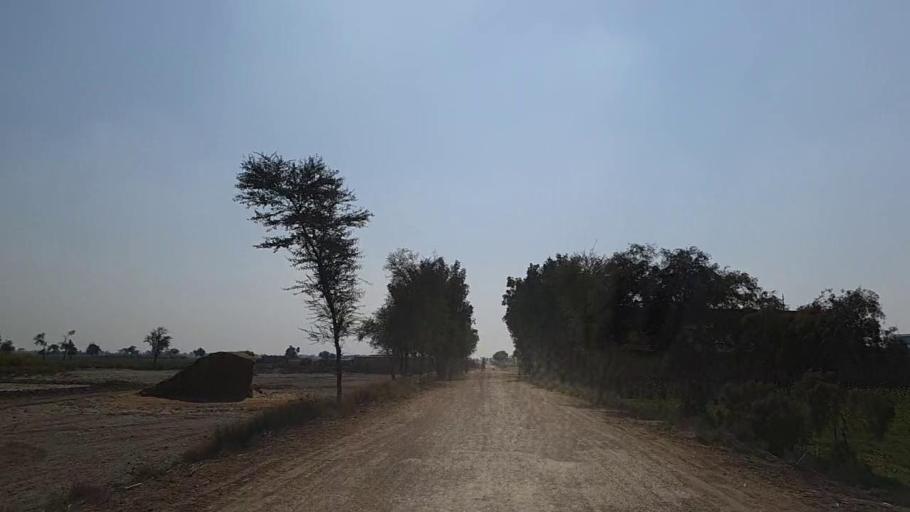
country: PK
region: Sindh
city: Daur
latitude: 26.4575
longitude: 68.2709
